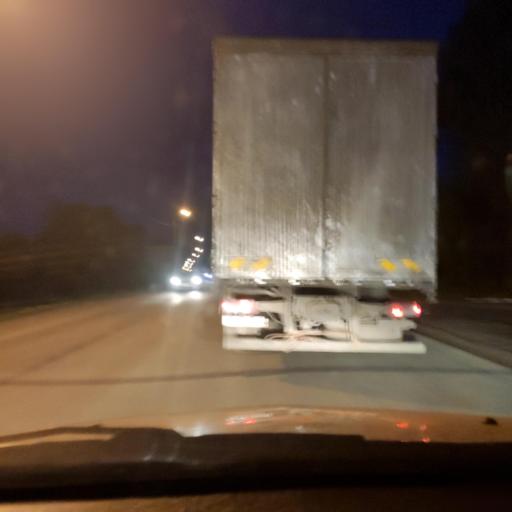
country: RU
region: Bashkortostan
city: Kabakovo
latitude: 54.6336
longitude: 56.0967
